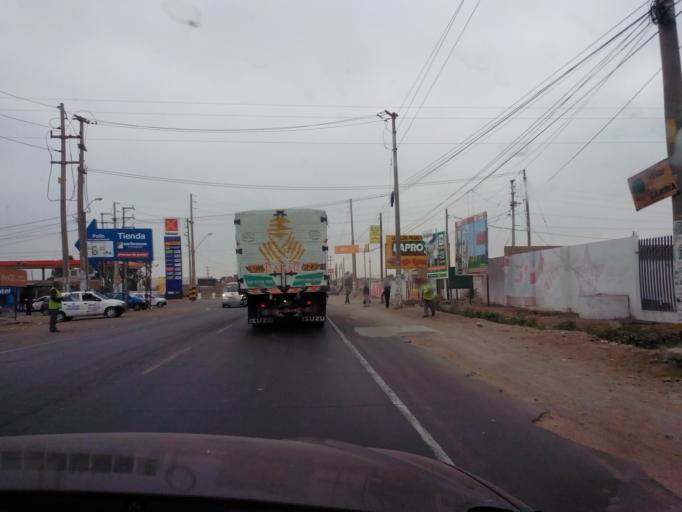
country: PE
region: Ica
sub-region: Provincia de Chincha
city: Chincha Baja
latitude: -13.4514
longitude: -76.1362
